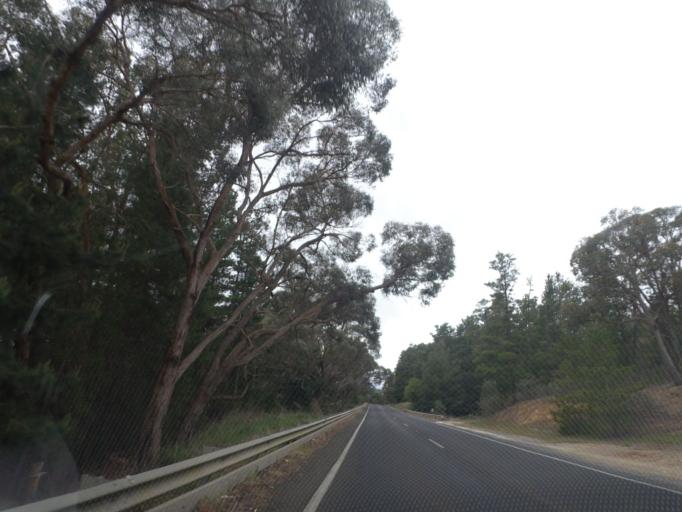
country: AU
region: Victoria
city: Brown Hill
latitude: -37.4146
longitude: 143.9088
